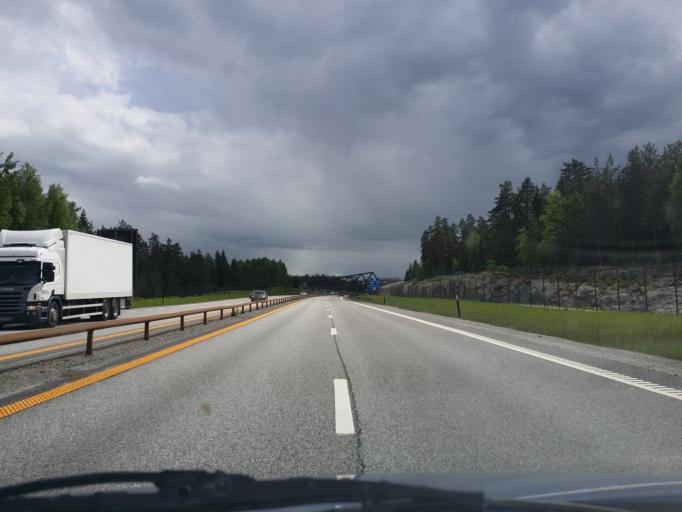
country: NO
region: Akershus
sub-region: Eidsvoll
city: Raholt
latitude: 60.3086
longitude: 11.1414
